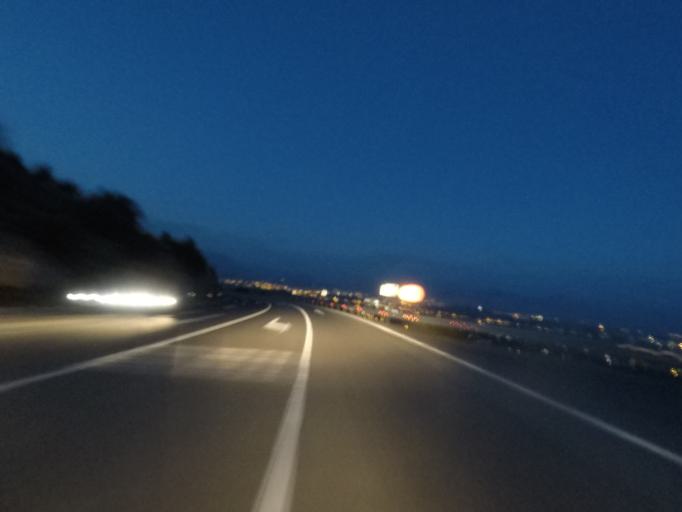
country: ME
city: Mojanovici
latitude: 42.4027
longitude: 19.1743
